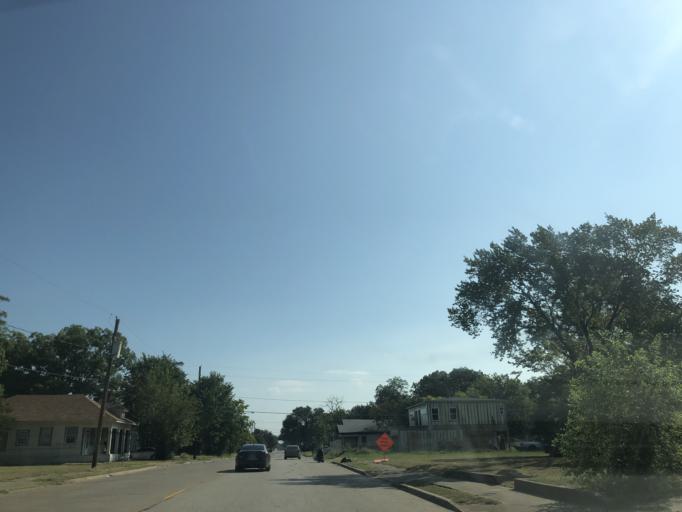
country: US
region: Texas
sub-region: Dallas County
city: Dallas
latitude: 32.7639
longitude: -96.7710
